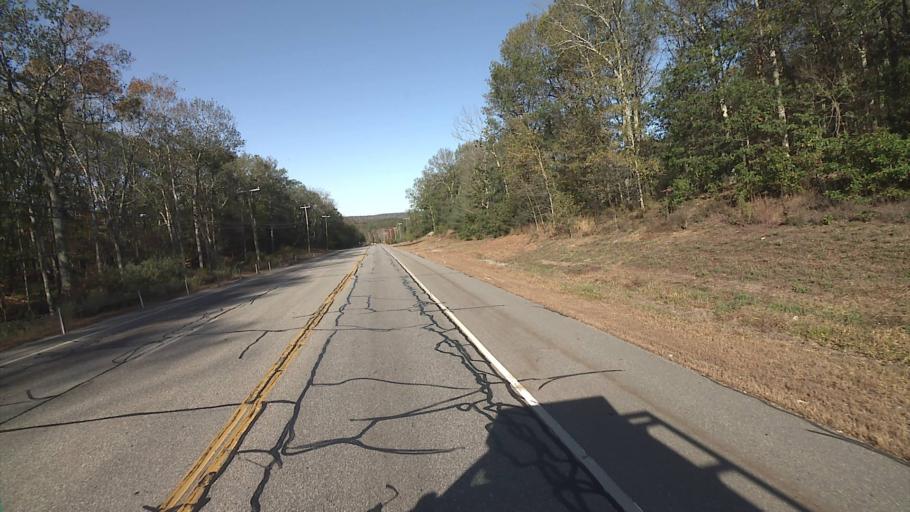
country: US
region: Connecticut
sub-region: Windham County
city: Windham
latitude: 41.7687
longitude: -72.1204
